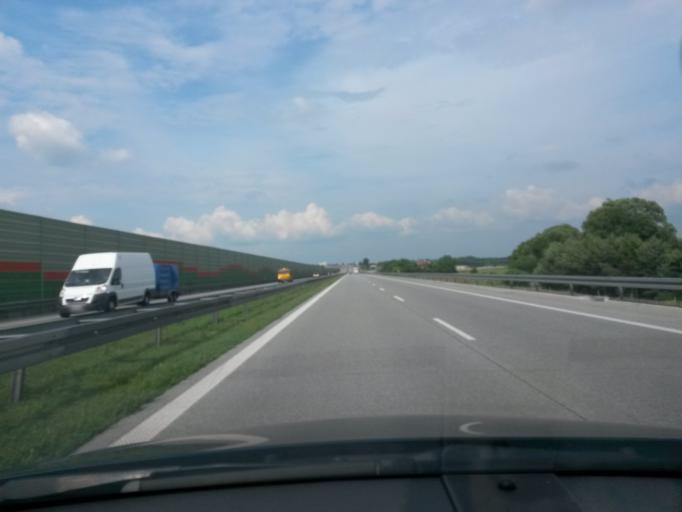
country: PL
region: Lodz Voivodeship
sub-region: Powiat tomaszowski
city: Tomaszow Mazowiecki
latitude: 51.5323
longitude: 19.9518
